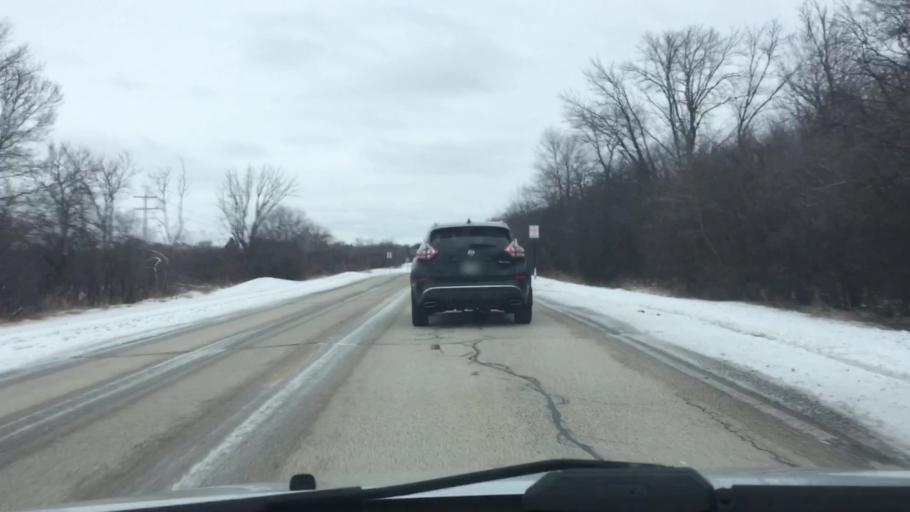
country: US
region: Wisconsin
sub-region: Waukesha County
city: Brookfield
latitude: 43.0474
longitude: -88.1060
